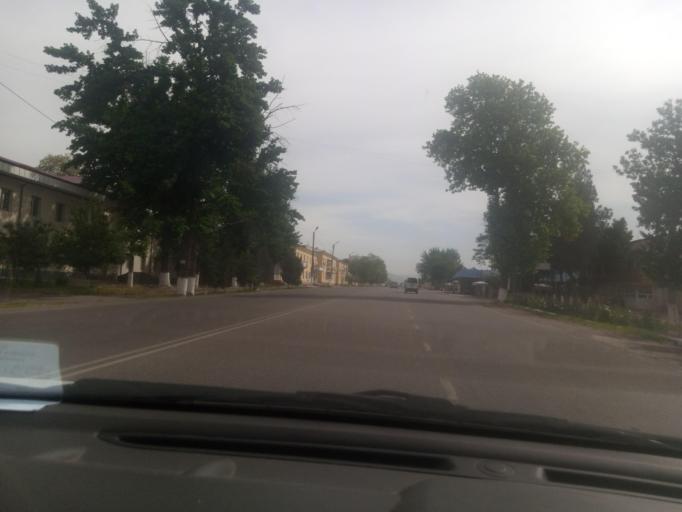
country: UZ
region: Toshkent
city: Angren
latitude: 41.0041
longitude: 70.0842
